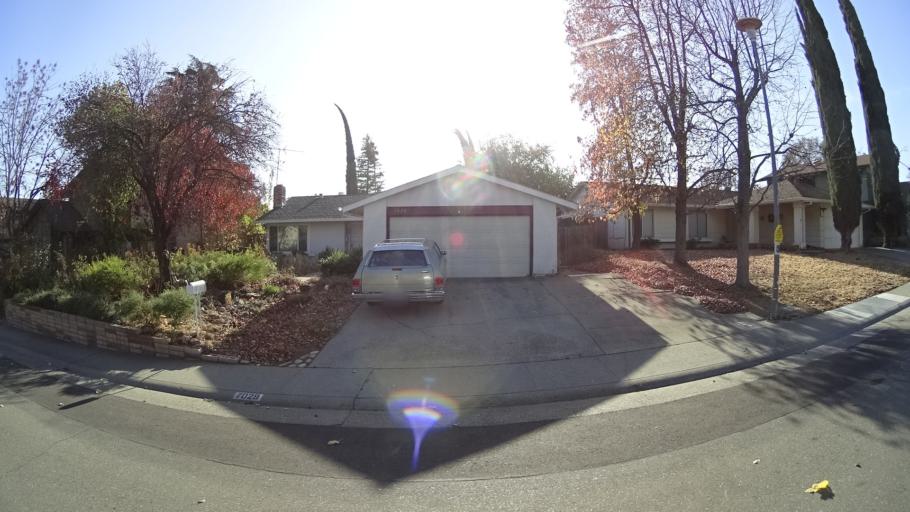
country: US
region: California
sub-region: Sacramento County
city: Antelope
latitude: 38.6969
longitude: -121.3150
